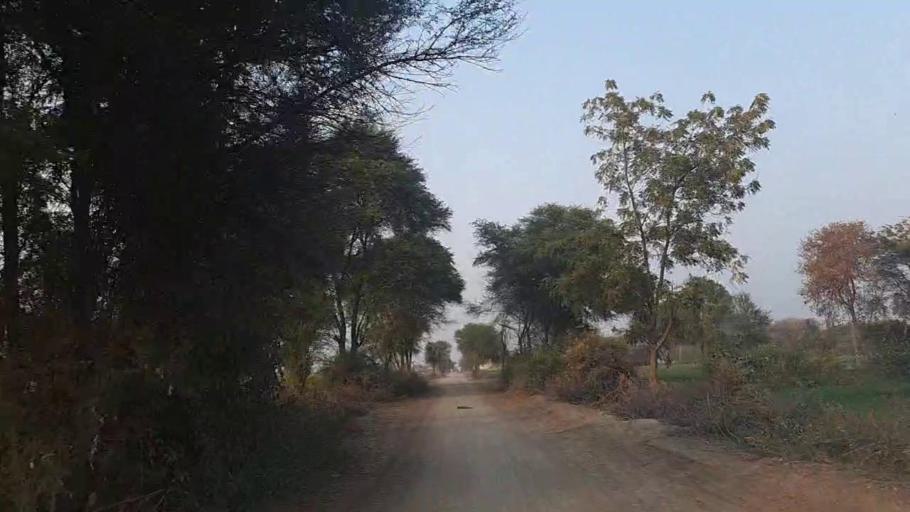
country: PK
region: Sindh
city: Nawabshah
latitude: 26.2782
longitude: 68.4648
